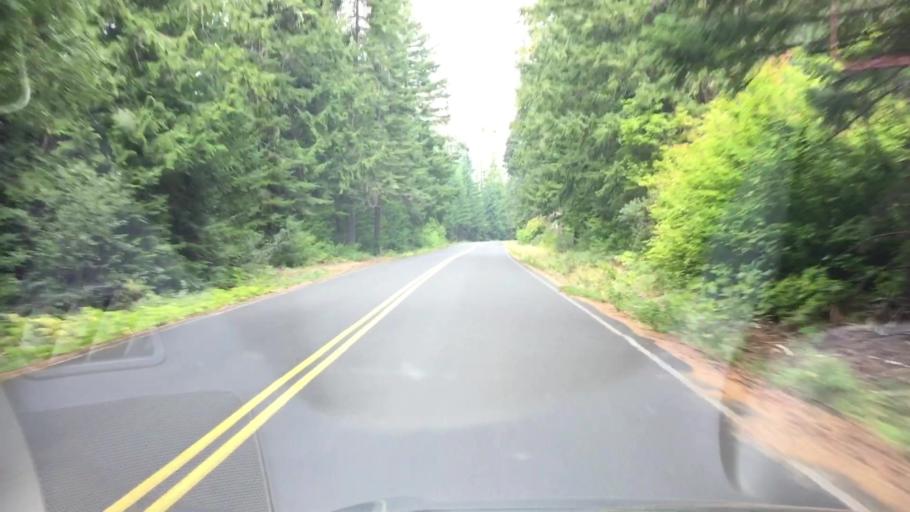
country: US
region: Washington
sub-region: Klickitat County
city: White Salmon
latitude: 46.0620
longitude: -121.5702
